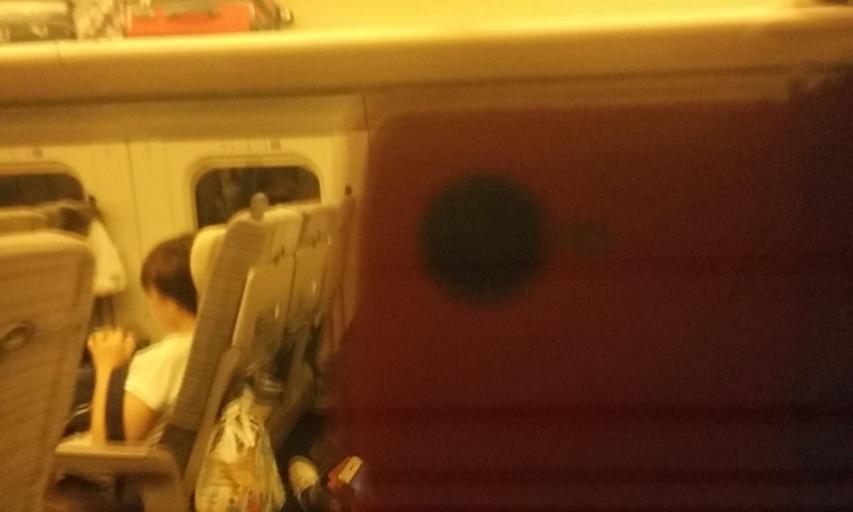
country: JP
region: Tochigi
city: Yaita
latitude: 36.8088
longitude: 139.9575
